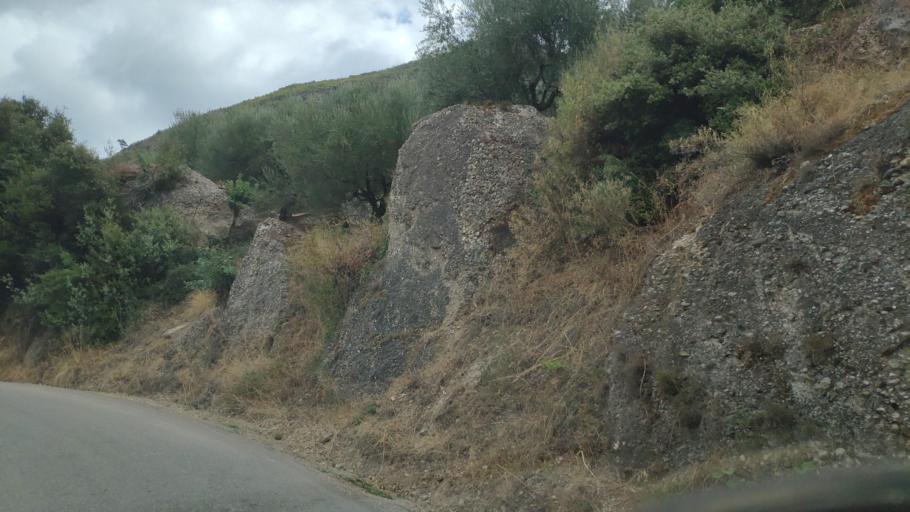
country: GR
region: West Greece
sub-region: Nomos Achaias
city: Temeni
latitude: 38.1671
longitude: 22.1387
